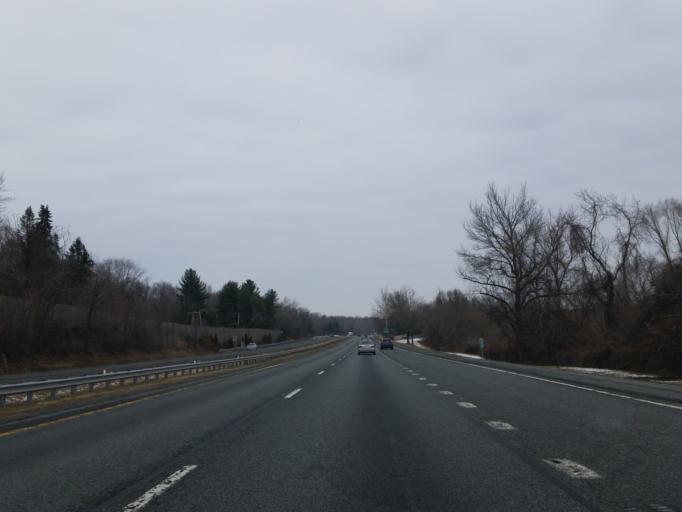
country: US
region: Maryland
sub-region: Baltimore County
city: Hunt Valley
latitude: 39.5431
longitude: -76.6664
